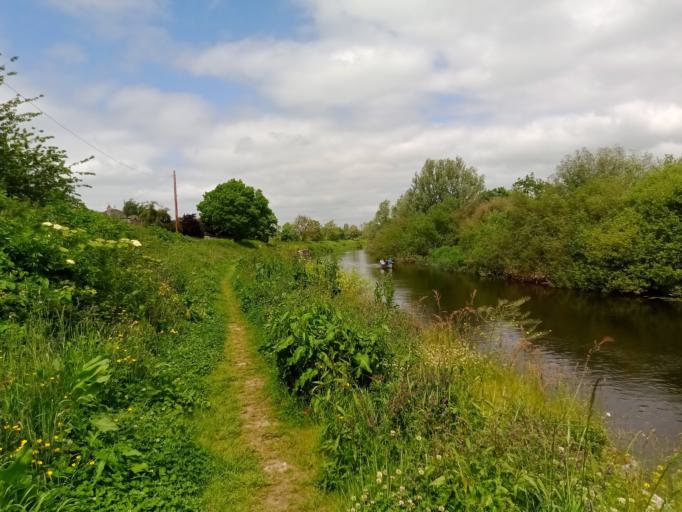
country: IE
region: Leinster
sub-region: County Carlow
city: Carlow
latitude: 52.8058
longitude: -6.9668
